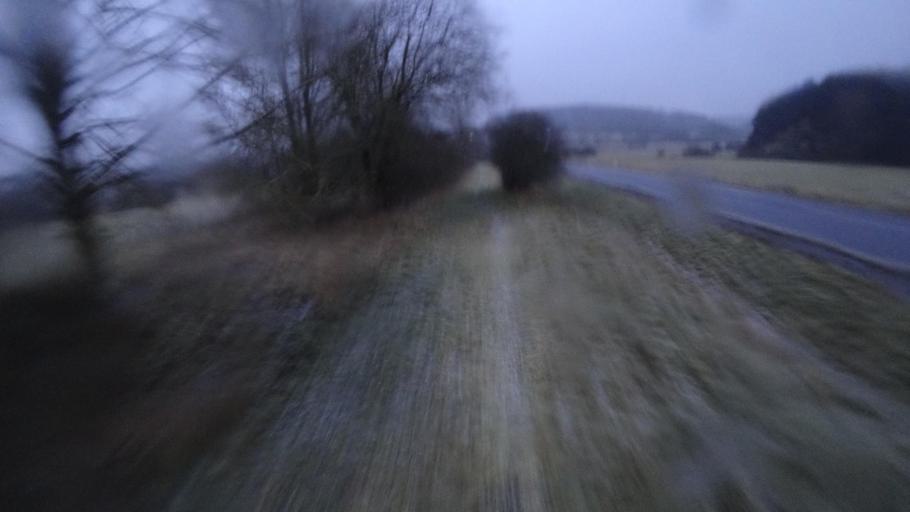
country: DE
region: Rheinland-Pfalz
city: Rotenhain
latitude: 50.5980
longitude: 7.8872
